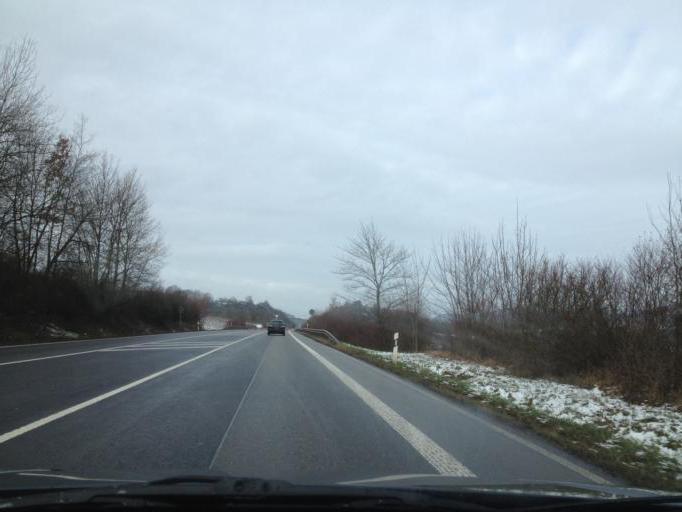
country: DE
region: Rheinland-Pfalz
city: Birkweiler
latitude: 49.2102
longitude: 8.0347
